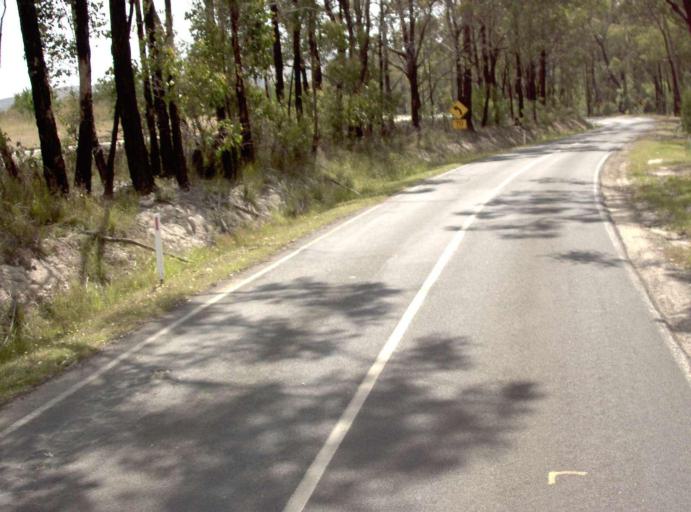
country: AU
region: Victoria
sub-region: Latrobe
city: Traralgon
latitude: -38.3071
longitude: 146.5537
